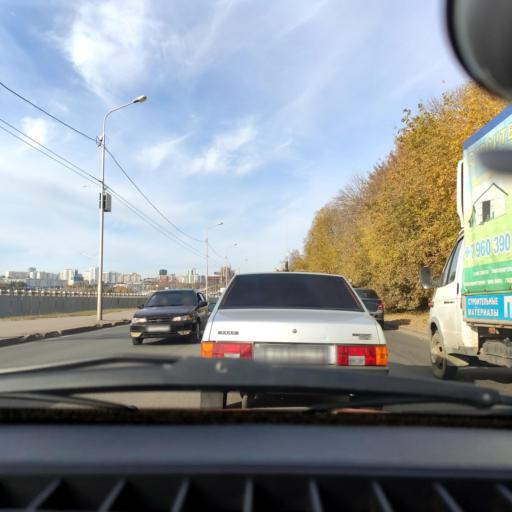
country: RU
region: Bashkortostan
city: Ufa
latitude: 54.7040
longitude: 55.9675
